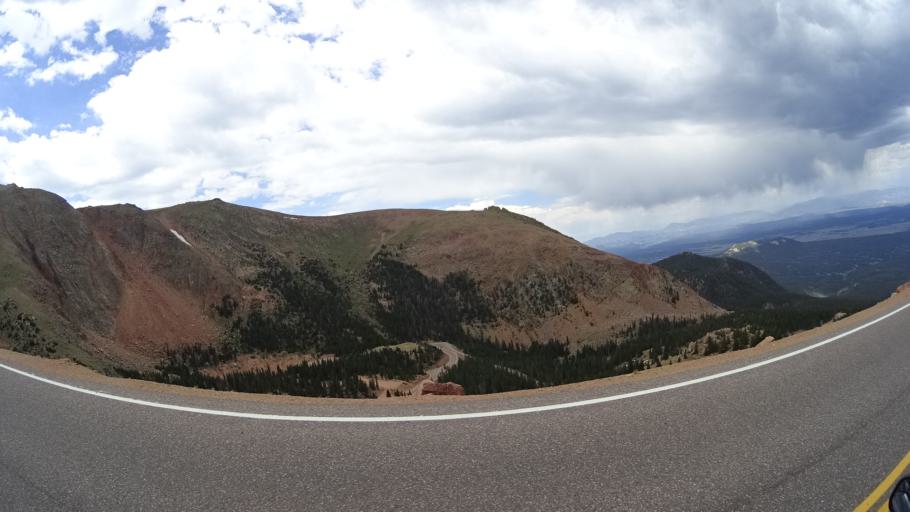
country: US
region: Colorado
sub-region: El Paso County
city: Cascade-Chipita Park
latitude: 38.8739
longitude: -105.0674
